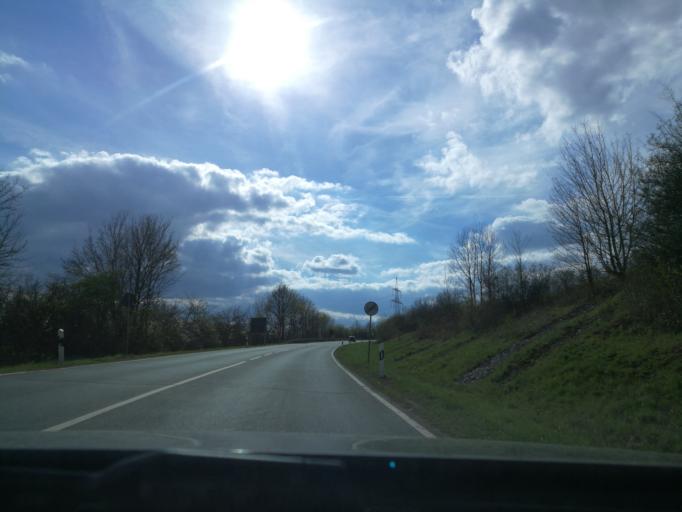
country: DE
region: Bavaria
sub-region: Upper Franconia
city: Weilersbach
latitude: 49.8071
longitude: 11.1103
